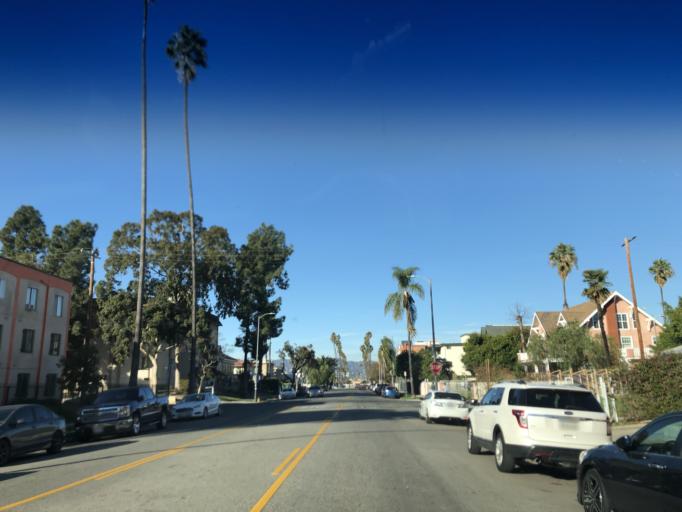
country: US
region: California
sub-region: Los Angeles County
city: Hollywood
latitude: 34.0449
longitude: -118.3145
